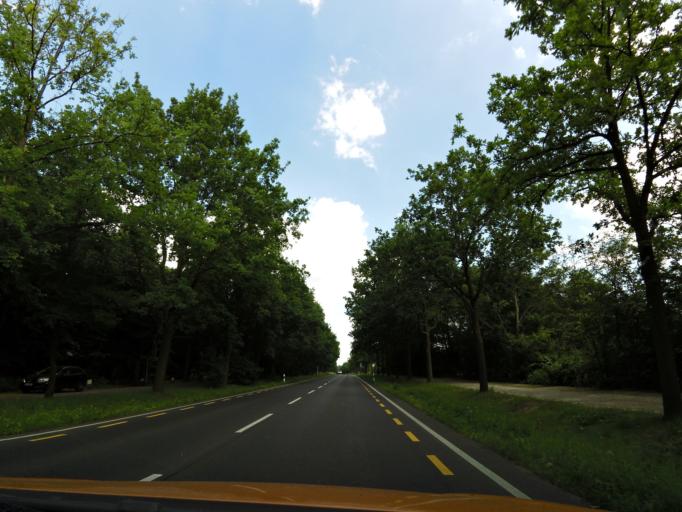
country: DE
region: Berlin
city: Wilhelmstadt
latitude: 52.5013
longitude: 13.1571
